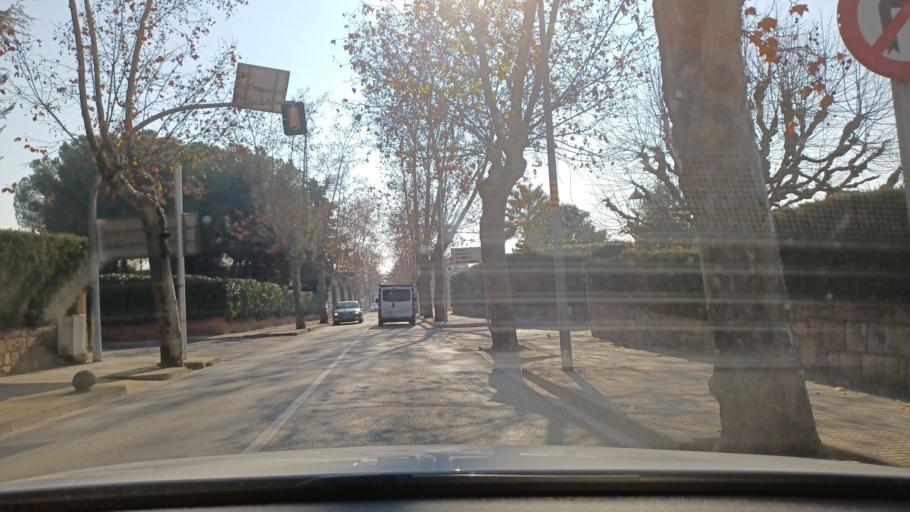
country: ES
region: Catalonia
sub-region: Provincia de Barcelona
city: L'Ametlla del Valles
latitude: 41.6652
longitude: 2.2661
